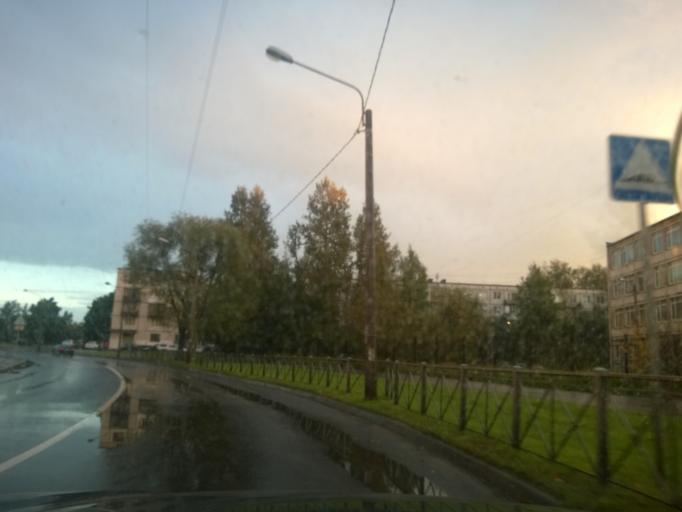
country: RU
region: St.-Petersburg
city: Uritsk
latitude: 59.8283
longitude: 30.1823
